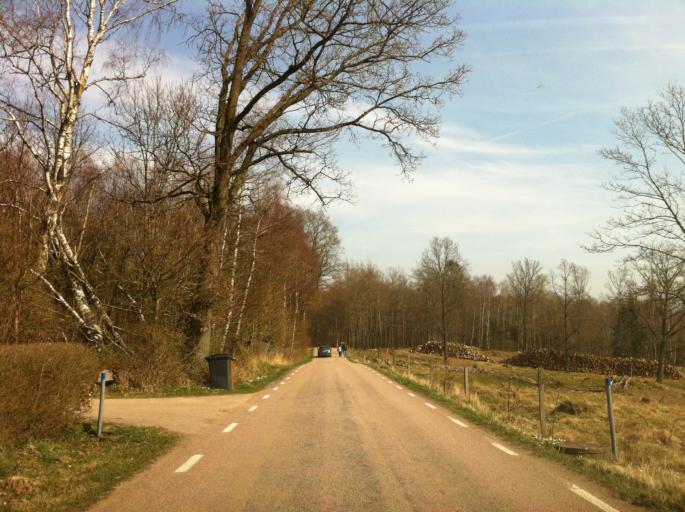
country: SE
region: Skane
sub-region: Klippans Kommun
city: Ljungbyhed
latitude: 55.9945
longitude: 13.2434
